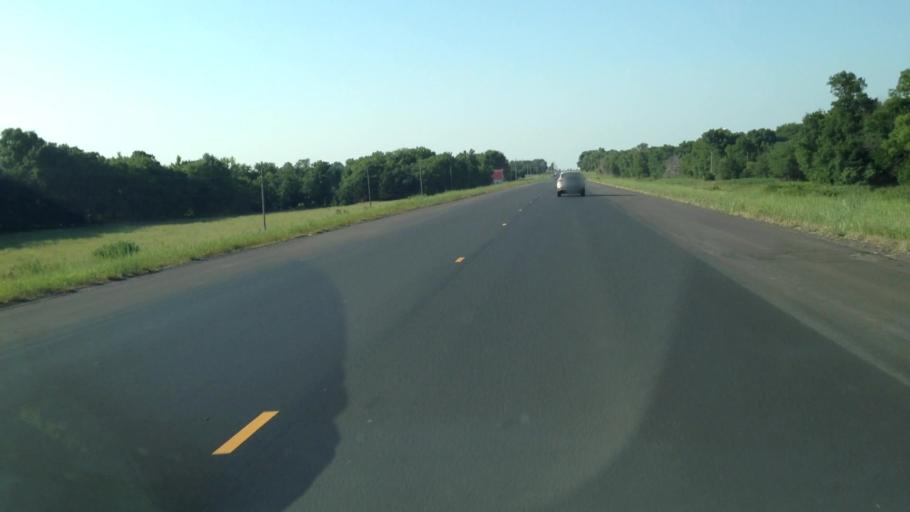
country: US
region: Kansas
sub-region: Franklin County
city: Ottawa
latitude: 38.4780
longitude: -95.2673
